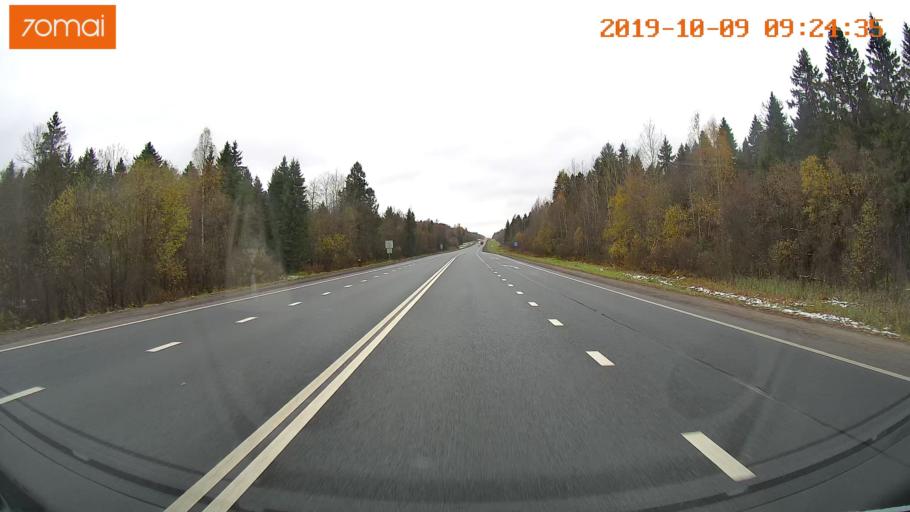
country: RU
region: Vologda
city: Vologda
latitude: 59.0804
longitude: 40.0142
